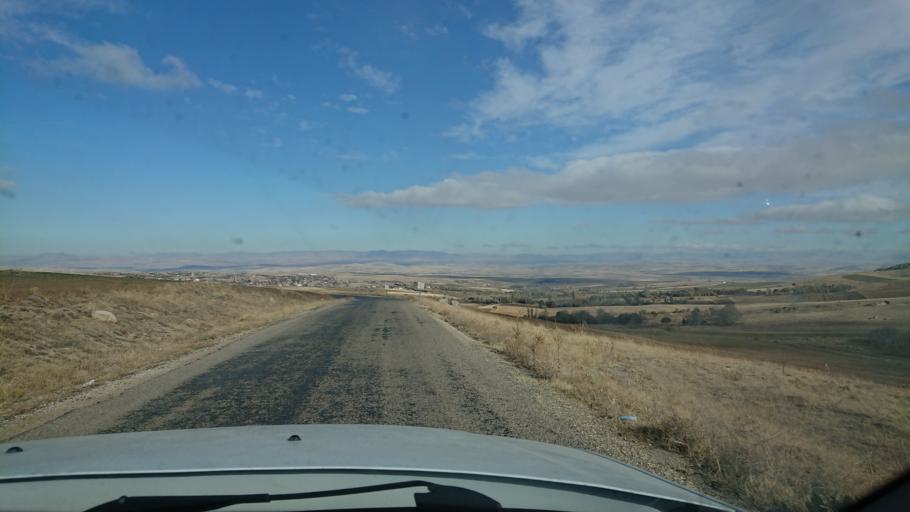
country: TR
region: Aksaray
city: Agacoren
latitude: 38.8422
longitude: 33.9527
